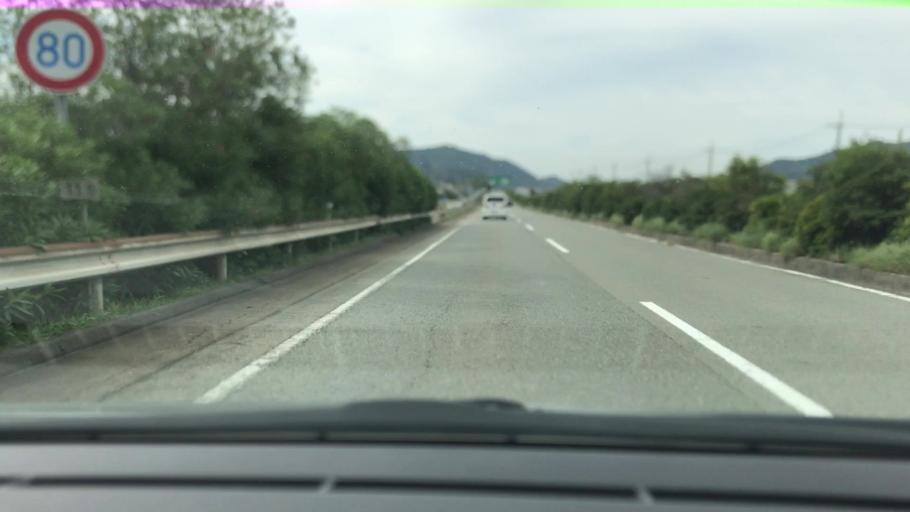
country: JP
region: Hyogo
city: Himeji
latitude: 34.8915
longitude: 134.7470
